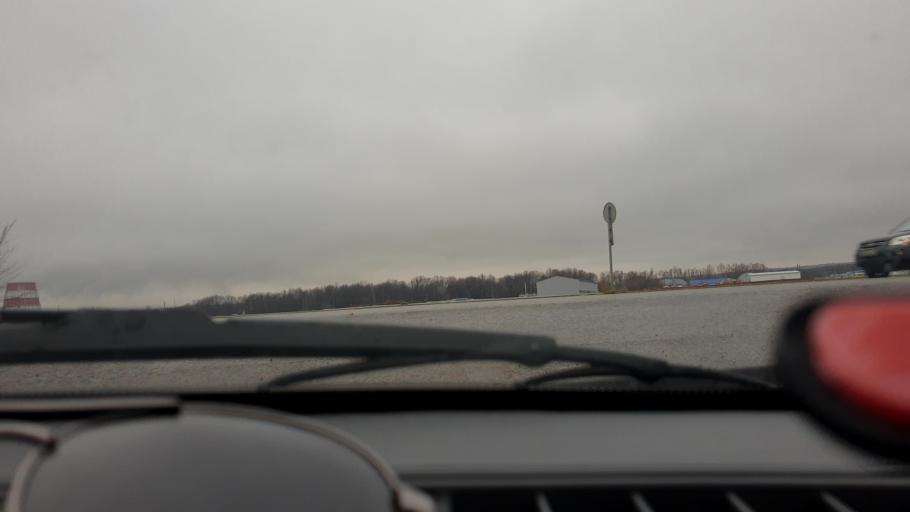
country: RU
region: Bashkortostan
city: Mikhaylovka
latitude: 54.7958
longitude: 55.8519
